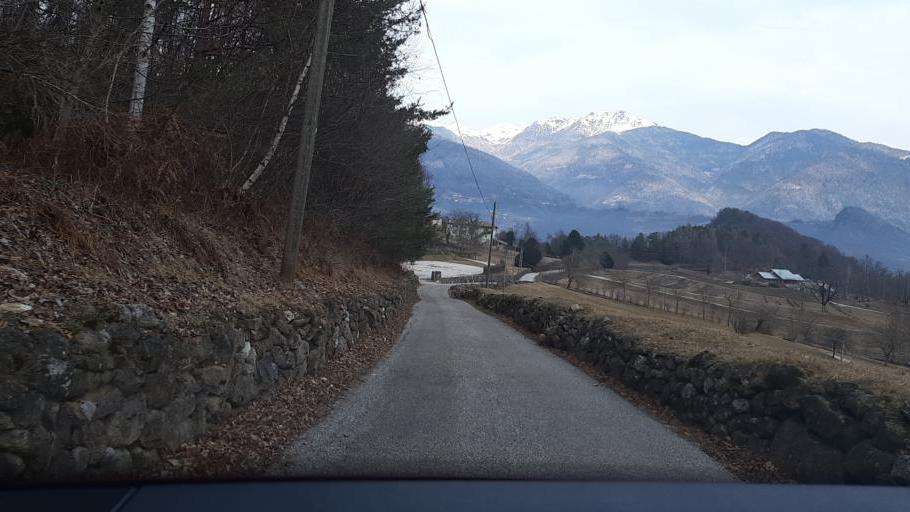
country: IT
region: Trentino-Alto Adige
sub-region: Provincia di Trento
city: Borgo
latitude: 46.0351
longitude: 11.4519
